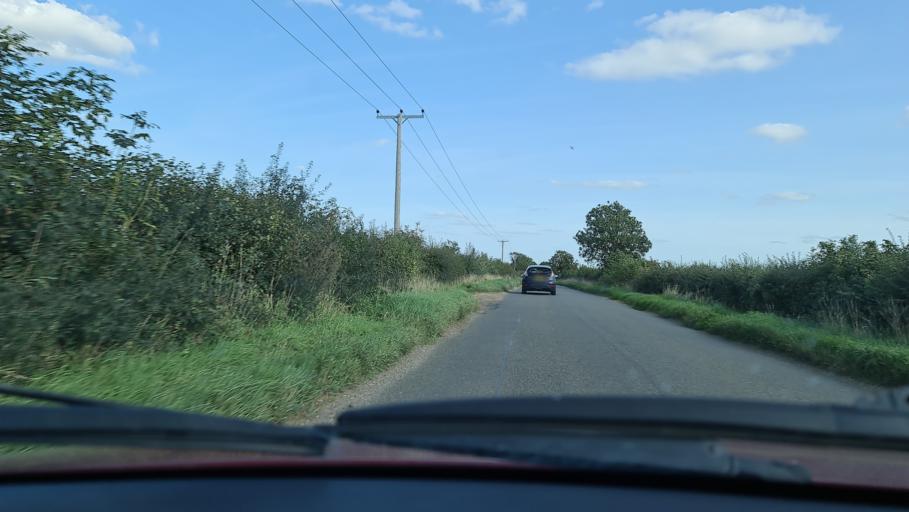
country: GB
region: England
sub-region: Northamptonshire
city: Brackley
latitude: 52.0144
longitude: -1.1710
